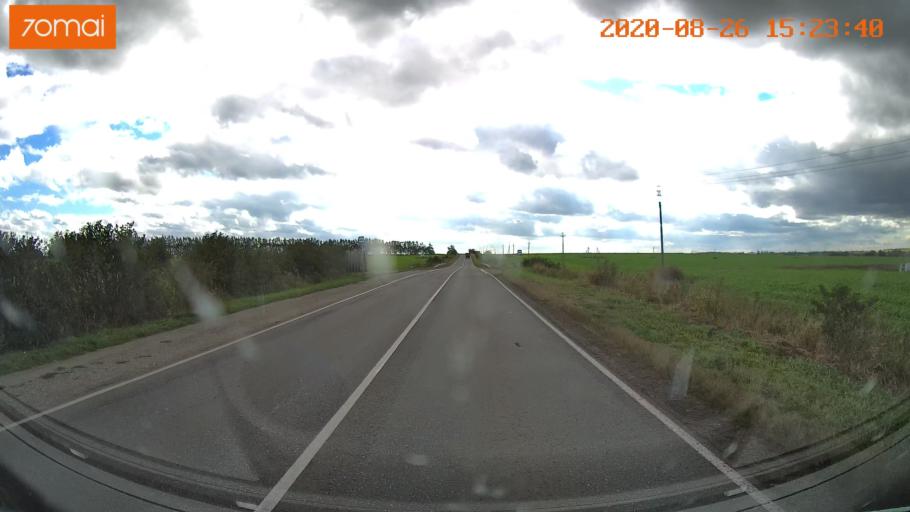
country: RU
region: Tula
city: Severo-Zadonsk
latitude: 54.1213
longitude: 38.4540
